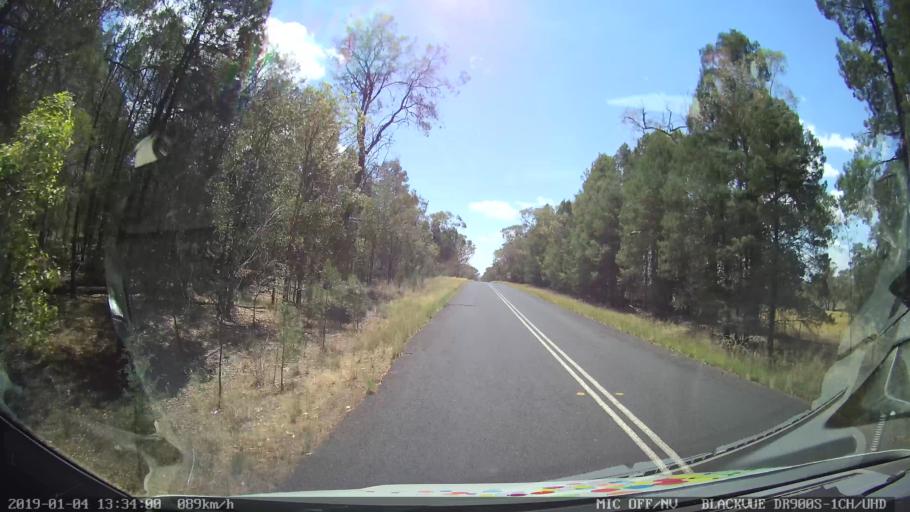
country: AU
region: New South Wales
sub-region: Dubbo Municipality
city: Dubbo
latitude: -32.5913
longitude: 148.5375
